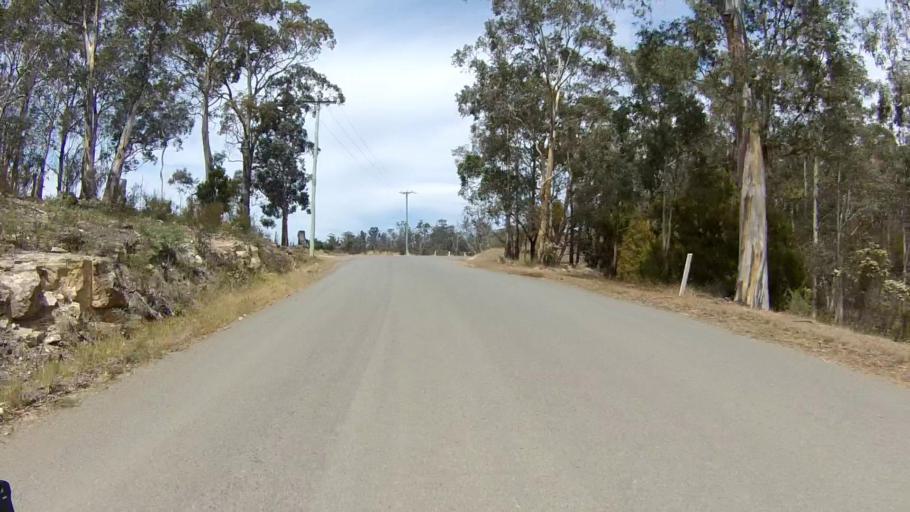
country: AU
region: Tasmania
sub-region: Sorell
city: Sorell
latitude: -42.7968
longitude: 147.6838
